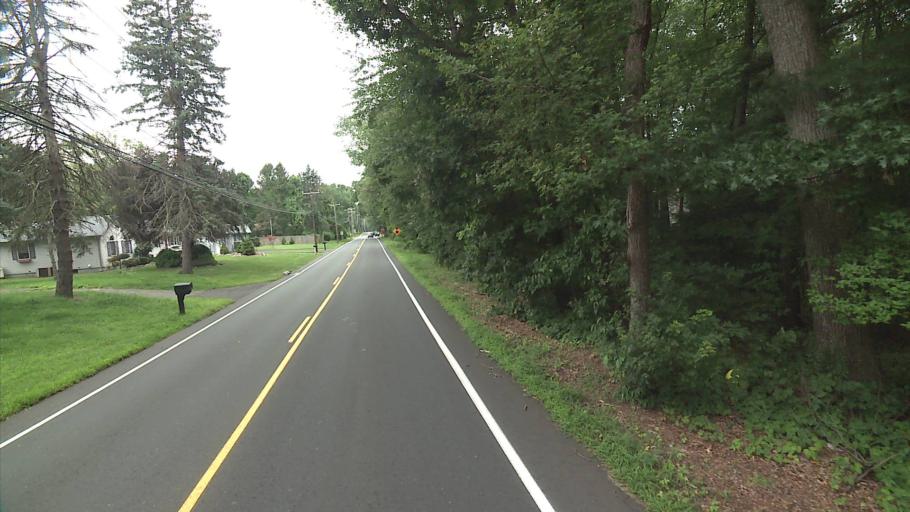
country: US
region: Connecticut
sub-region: Hartford County
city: Broad Brook
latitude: 41.8491
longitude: -72.5237
